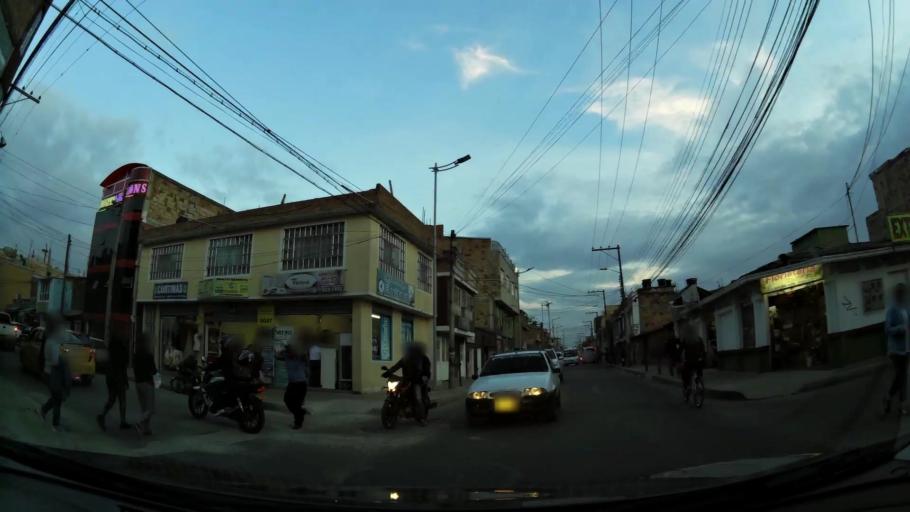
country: CO
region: Cundinamarca
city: Funza
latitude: 4.7141
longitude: -74.2150
